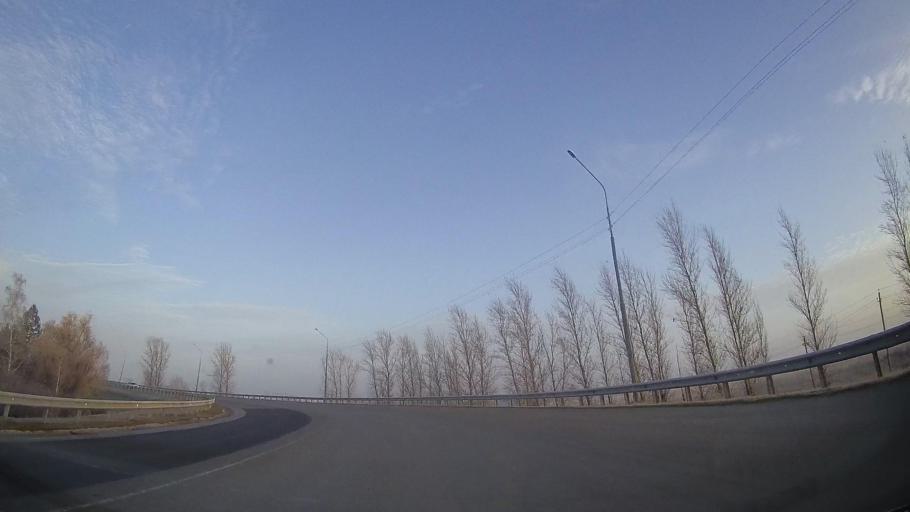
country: RU
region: Rostov
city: Bataysk
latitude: 47.1021
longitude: 39.7667
